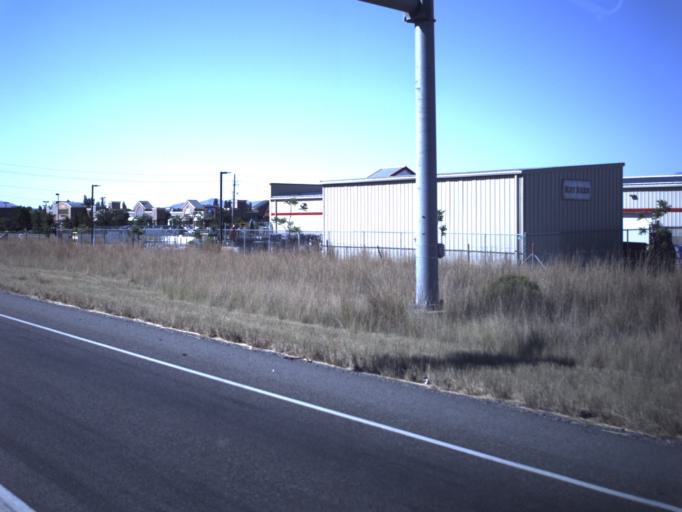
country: US
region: Utah
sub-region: Tooele County
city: Stansbury park
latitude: 40.6546
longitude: -112.2895
